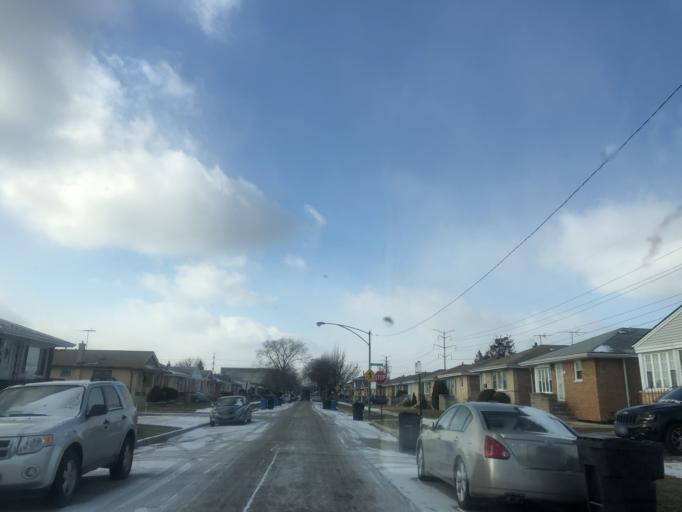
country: US
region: Illinois
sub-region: Cook County
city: Hometown
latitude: 41.7565
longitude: -87.7178
